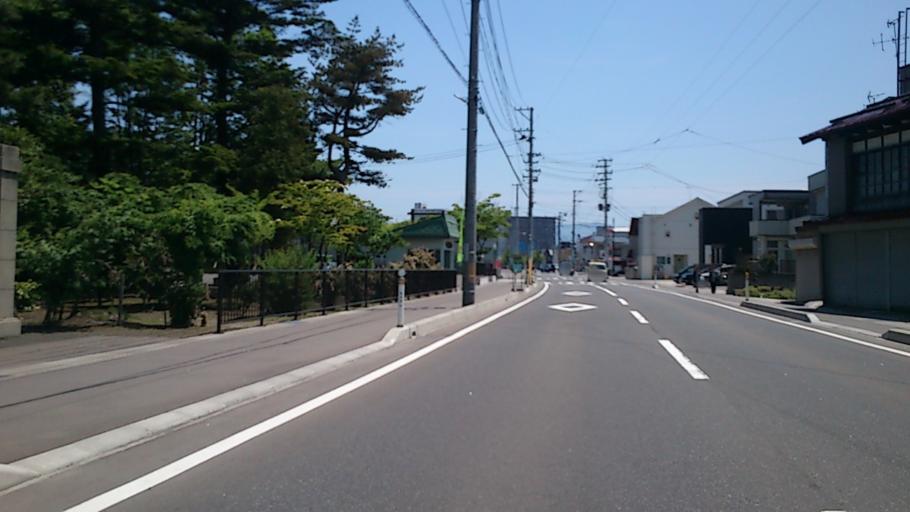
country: JP
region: Aomori
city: Aomori Shi
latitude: 40.8313
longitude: 140.7253
